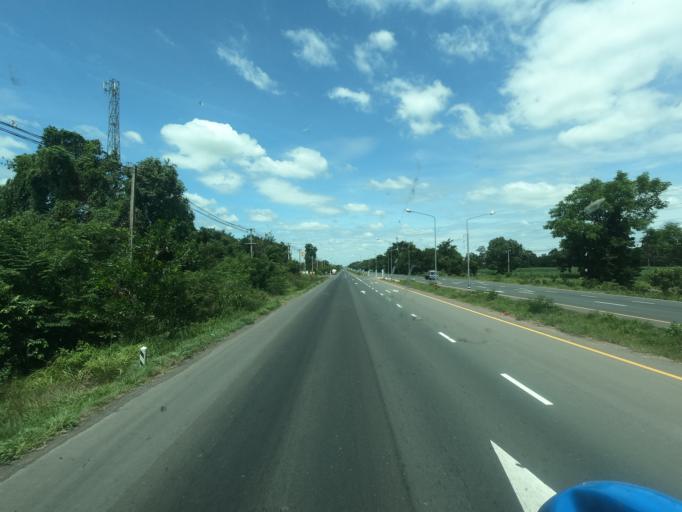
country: TH
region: Surin
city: Prasat
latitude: 14.6223
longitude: 103.3769
